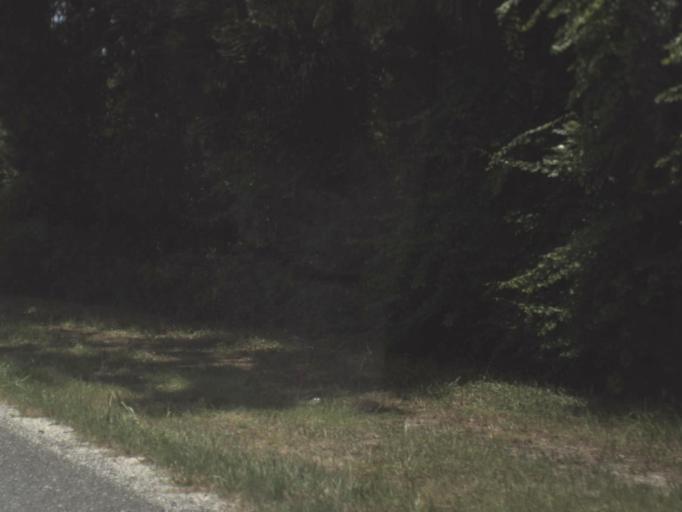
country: US
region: Florida
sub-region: Dixie County
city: Cross City
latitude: 29.6420
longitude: -83.1454
